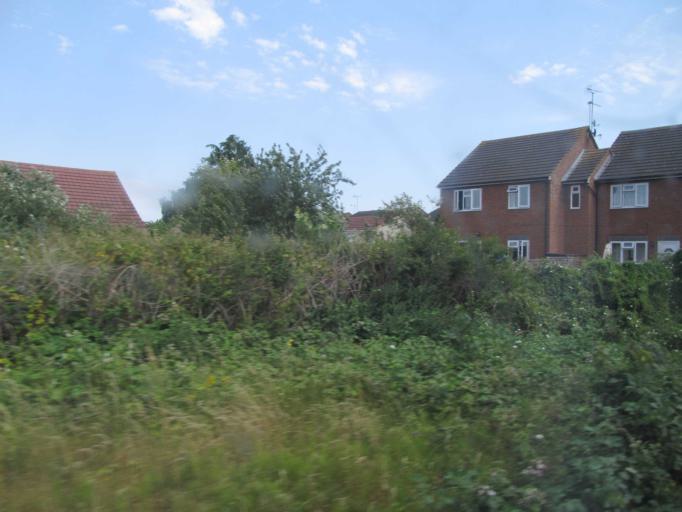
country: GB
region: England
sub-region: Buckinghamshire
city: Farnham Royal
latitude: 51.5239
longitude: -0.6523
